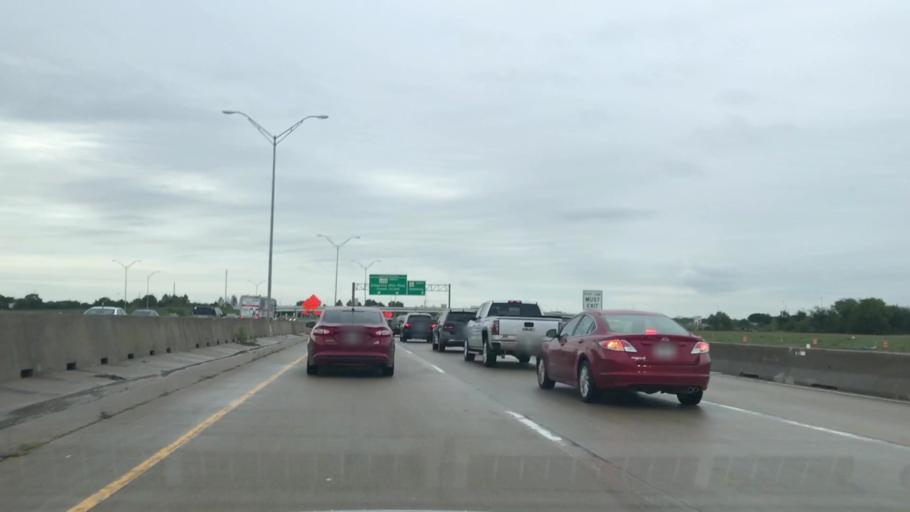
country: US
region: Texas
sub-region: Dallas County
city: Coppell
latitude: 32.9570
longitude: -97.0398
